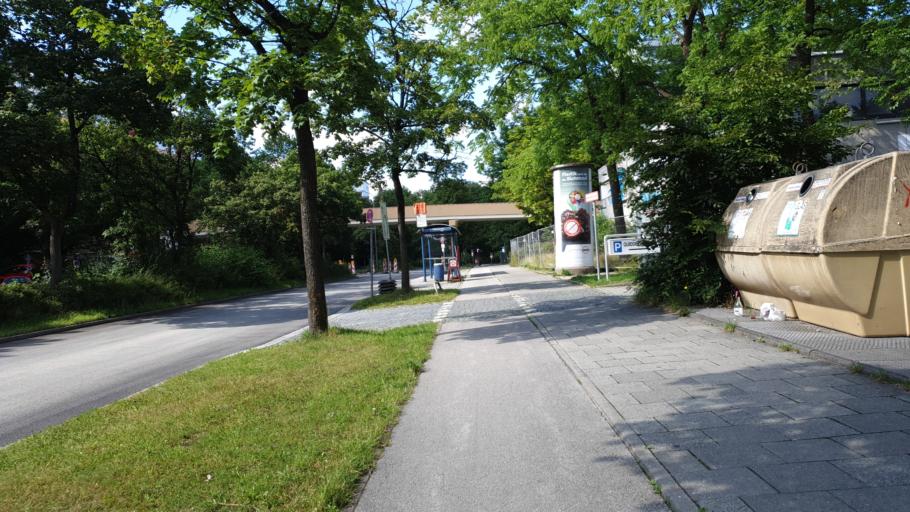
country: DE
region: Bavaria
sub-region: Upper Bavaria
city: Neubiberg
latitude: 48.1072
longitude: 11.6367
